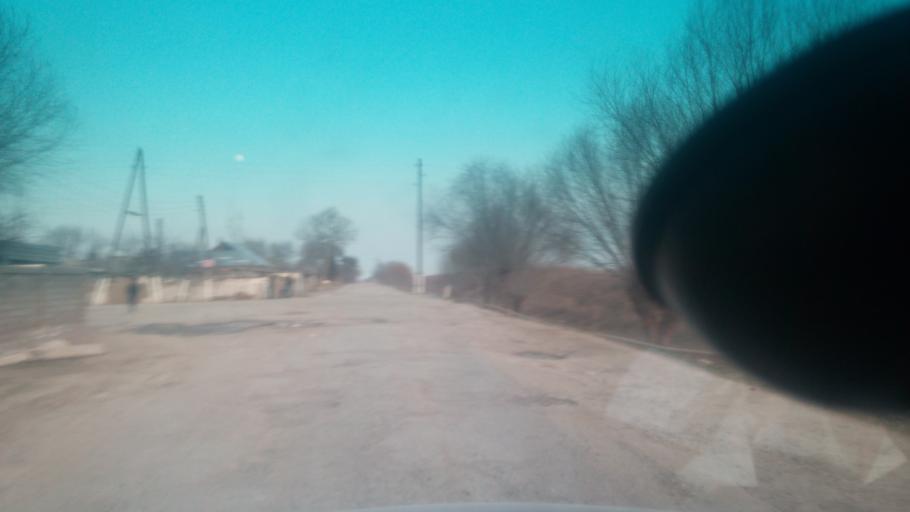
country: UZ
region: Sirdaryo
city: Guliston
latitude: 40.5365
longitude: 68.7957
